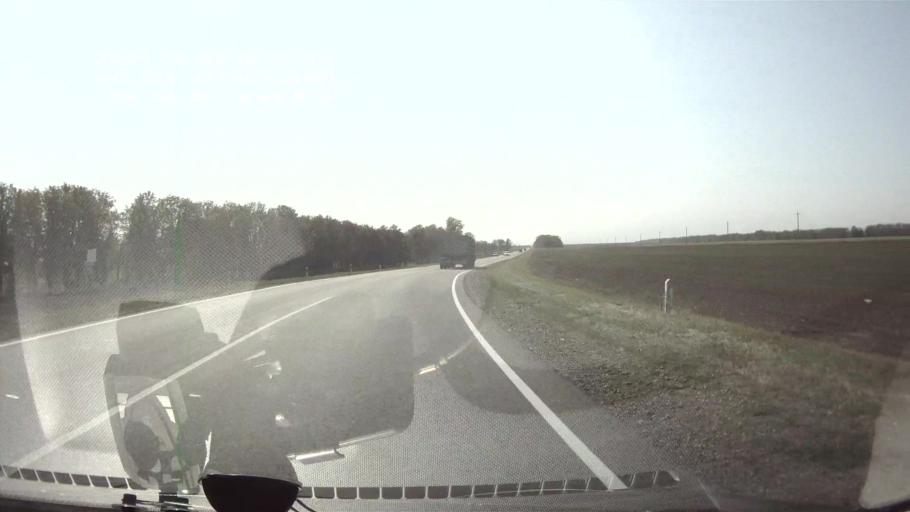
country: RU
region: Krasnodarskiy
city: Novopokrovskaya
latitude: 45.9075
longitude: 40.7210
